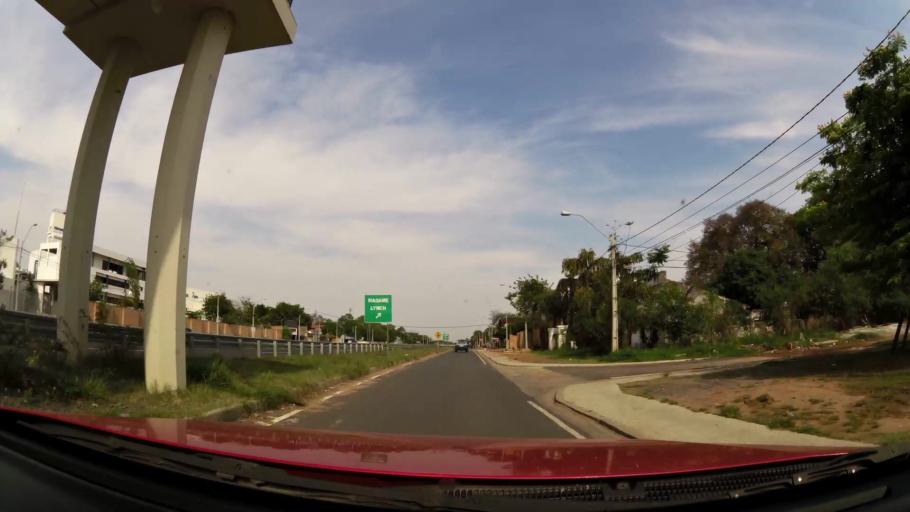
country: PY
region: Central
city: Fernando de la Mora
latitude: -25.2564
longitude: -57.5523
